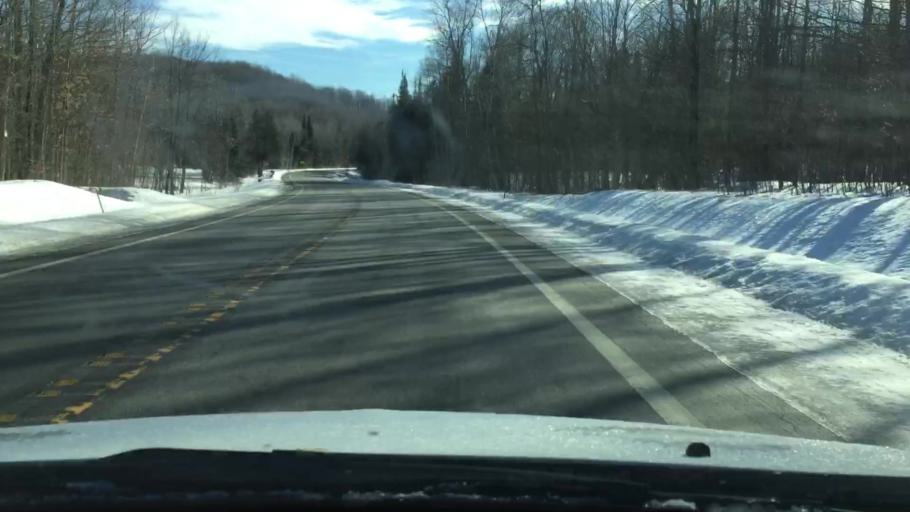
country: US
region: Michigan
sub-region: Antrim County
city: Mancelona
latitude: 45.0079
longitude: -85.0644
